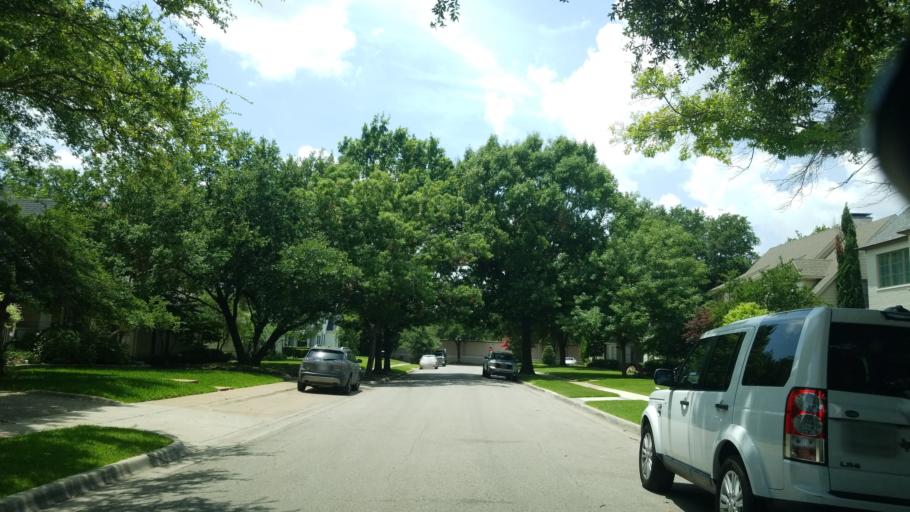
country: US
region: Texas
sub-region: Dallas County
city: University Park
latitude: 32.8559
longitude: -96.8112
